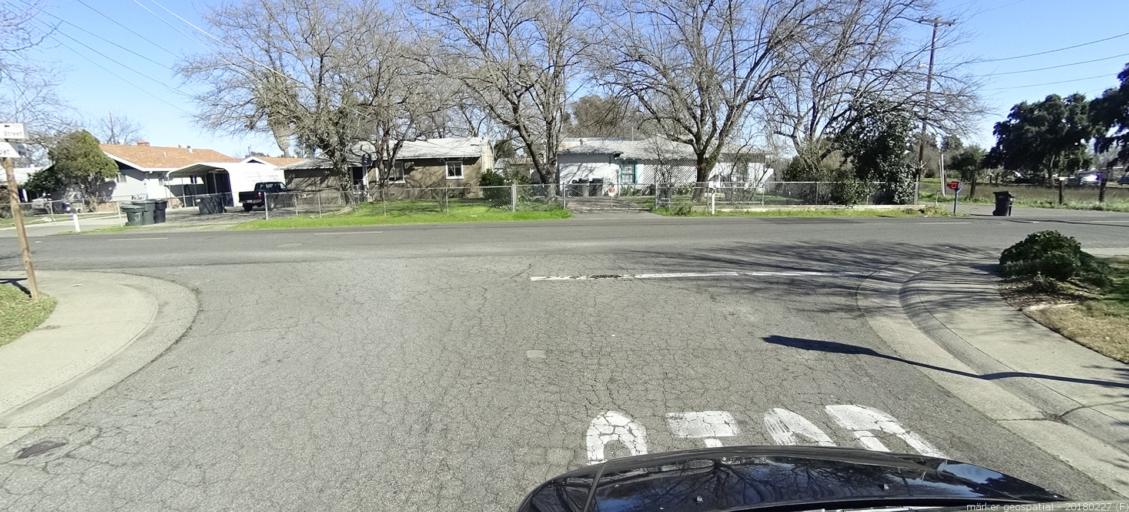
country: US
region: California
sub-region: Sacramento County
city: Rio Linda
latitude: 38.7003
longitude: -121.4432
